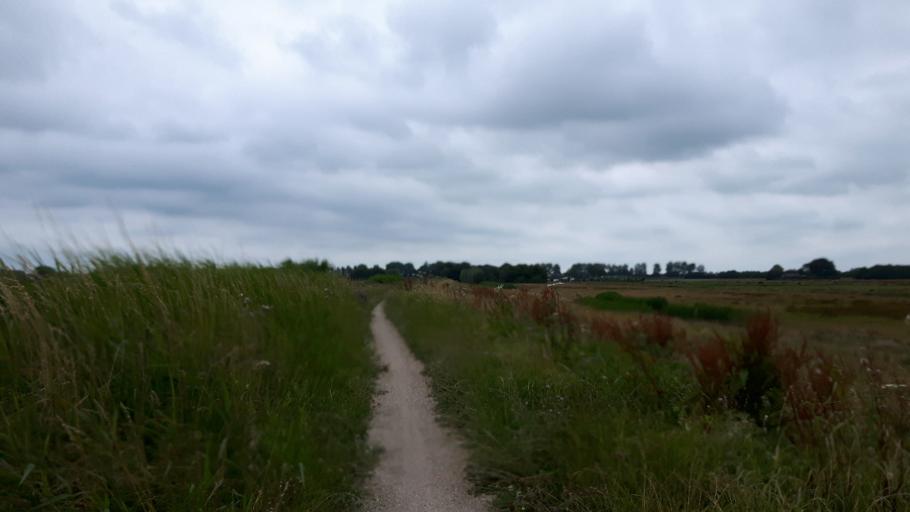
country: NL
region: South Holland
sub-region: Gemeente Pijnacker-Nootdorp
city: Pijnacker
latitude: 51.9717
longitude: 4.4161
